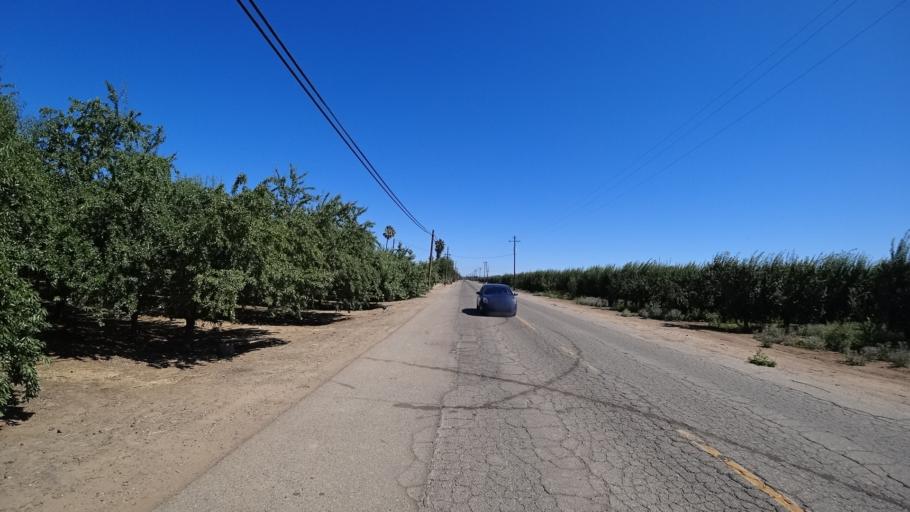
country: US
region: California
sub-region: Fresno County
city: West Park
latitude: 36.6967
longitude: -119.8089
